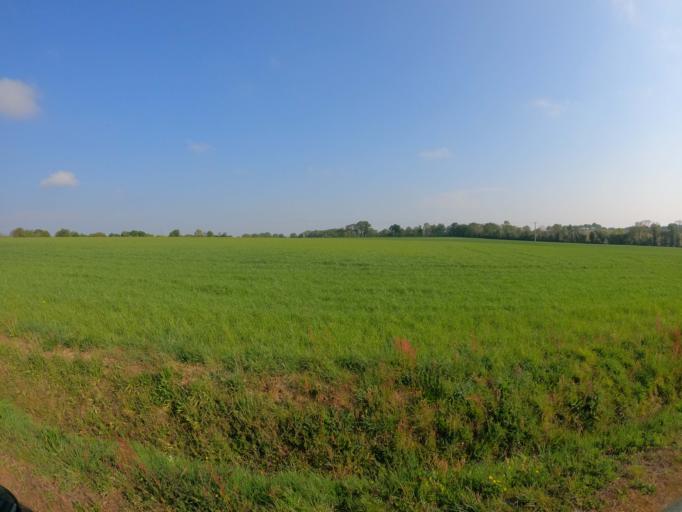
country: FR
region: Pays de la Loire
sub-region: Departement de Maine-et-Loire
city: La Seguiniere
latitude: 47.0714
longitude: -0.9728
